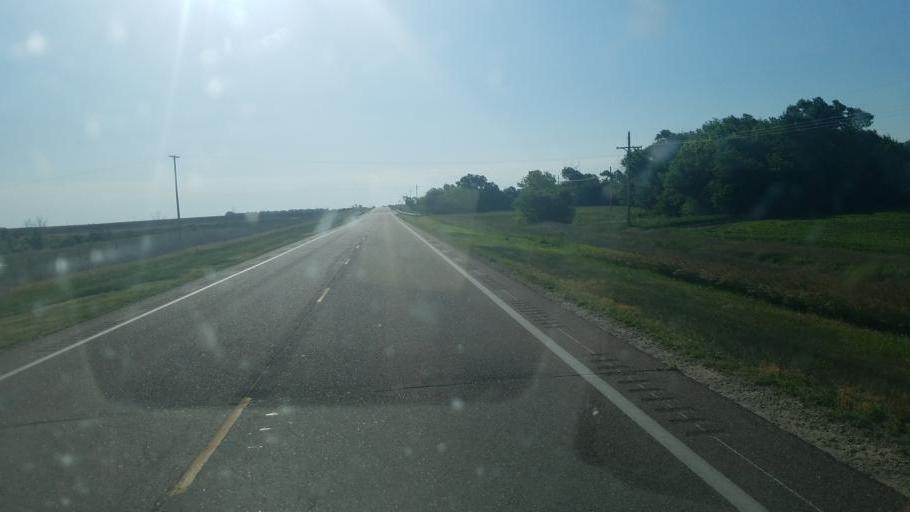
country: US
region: Kansas
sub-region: Pawnee County
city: Larned
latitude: 38.1897
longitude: -99.3262
